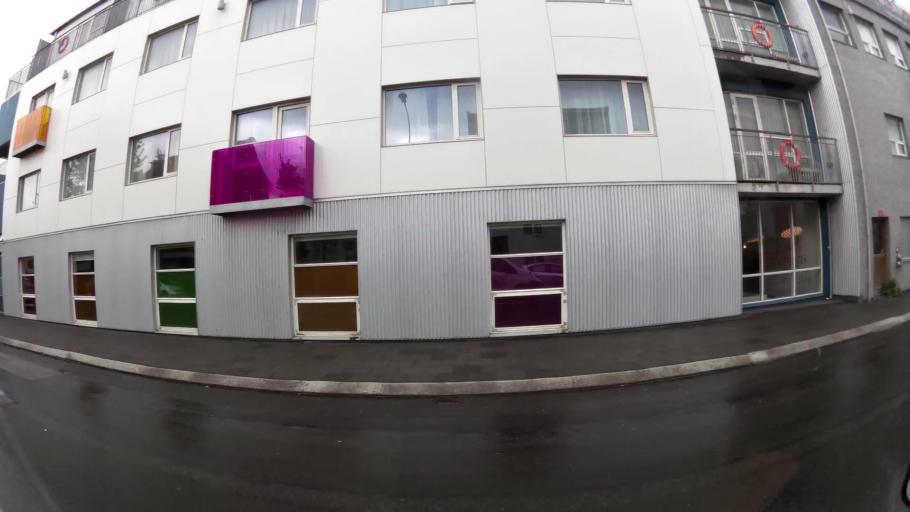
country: IS
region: Capital Region
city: Seltjarnarnes
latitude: 64.1511
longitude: -21.9472
